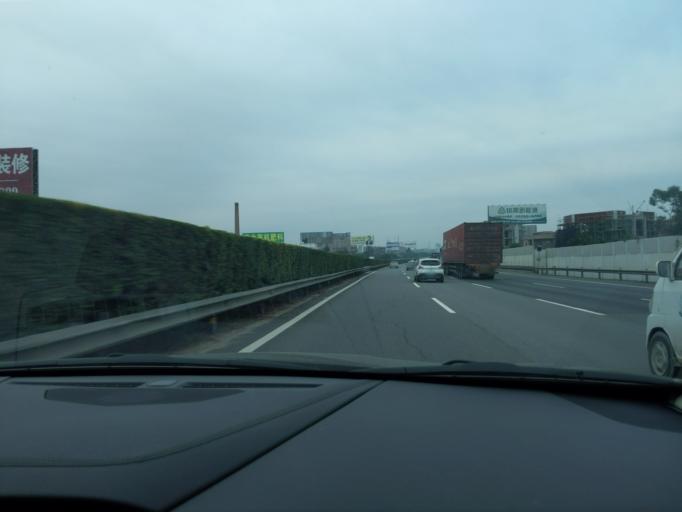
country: CN
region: Fujian
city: Anhai
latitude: 24.7417
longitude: 118.4257
